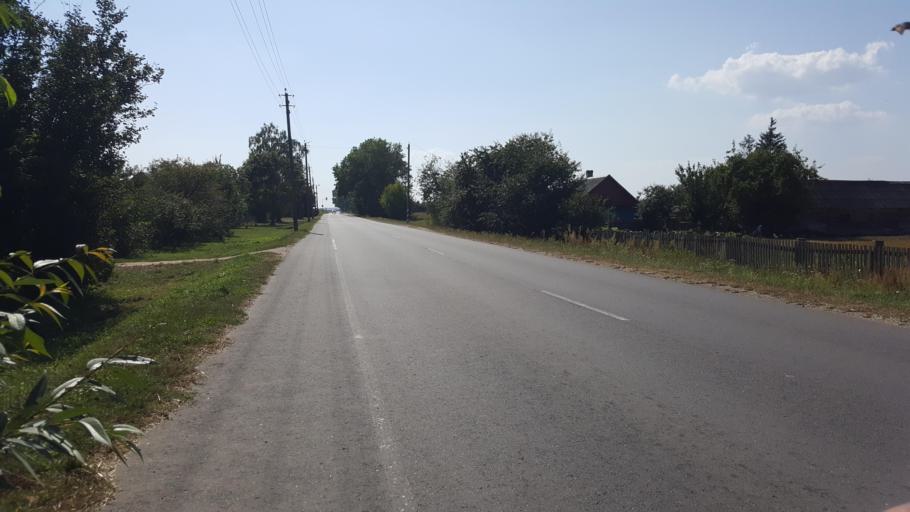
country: PL
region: Podlasie
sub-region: Powiat hajnowski
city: Czeremcha
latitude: 52.4920
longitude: 23.5559
